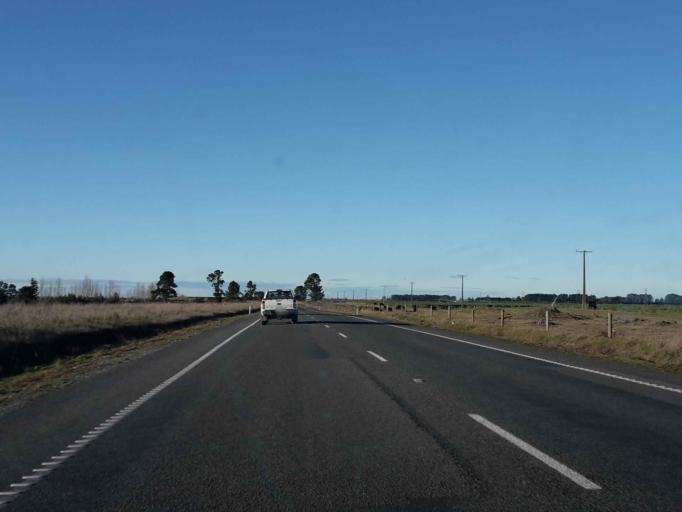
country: NZ
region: Canterbury
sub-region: Ashburton District
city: Tinwald
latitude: -44.0271
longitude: 171.4890
